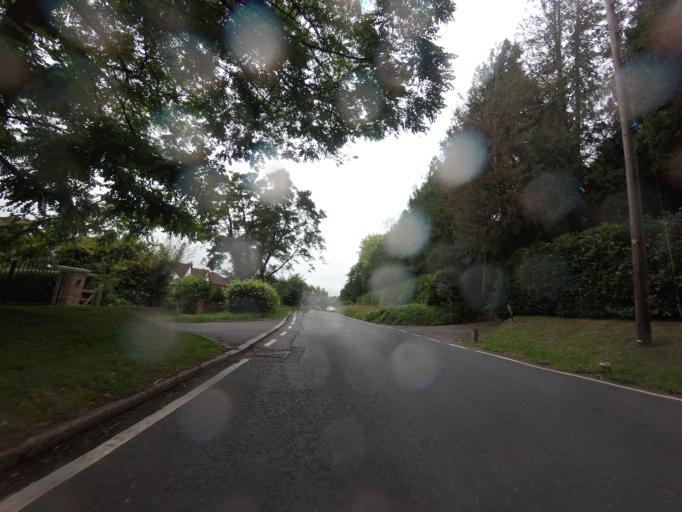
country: GB
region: England
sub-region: Kent
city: Kemsing
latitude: 51.3099
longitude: 0.2177
